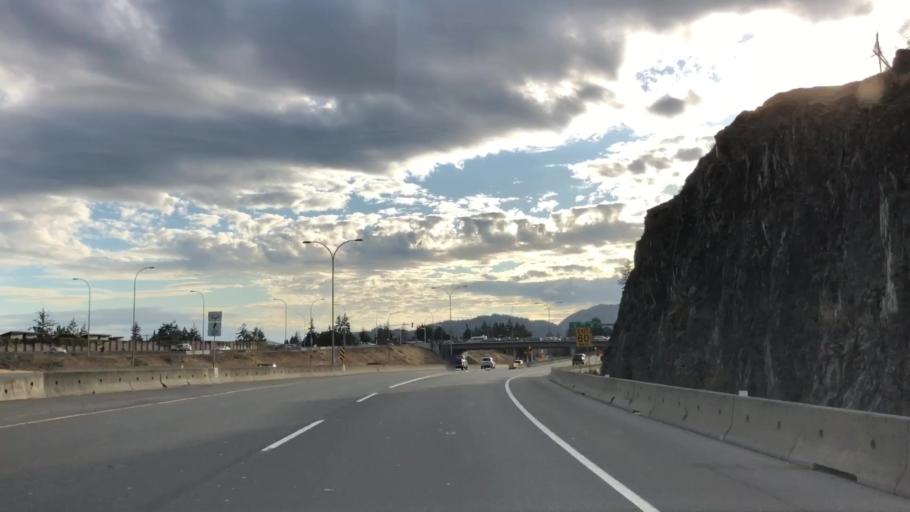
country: CA
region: British Columbia
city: Langford
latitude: 48.4578
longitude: -123.4939
